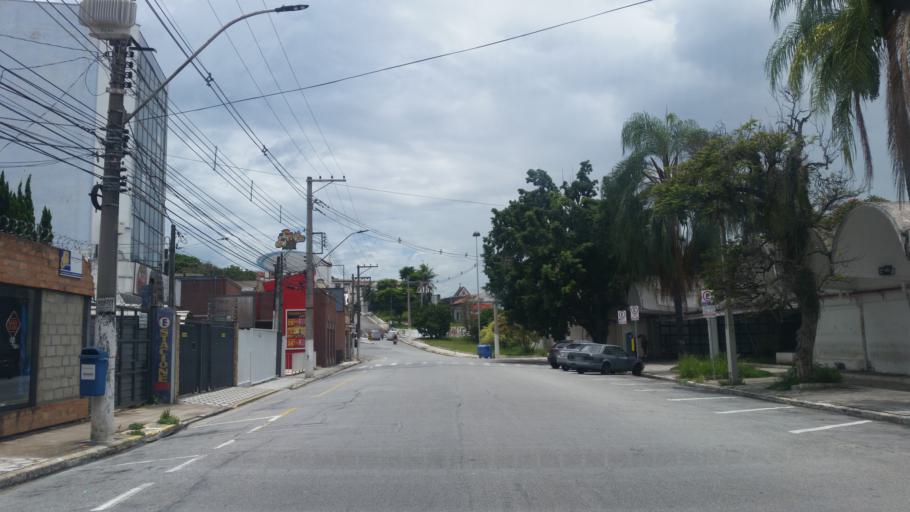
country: BR
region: Sao Paulo
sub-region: Taubate
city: Taubate
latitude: -23.0224
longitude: -45.5526
